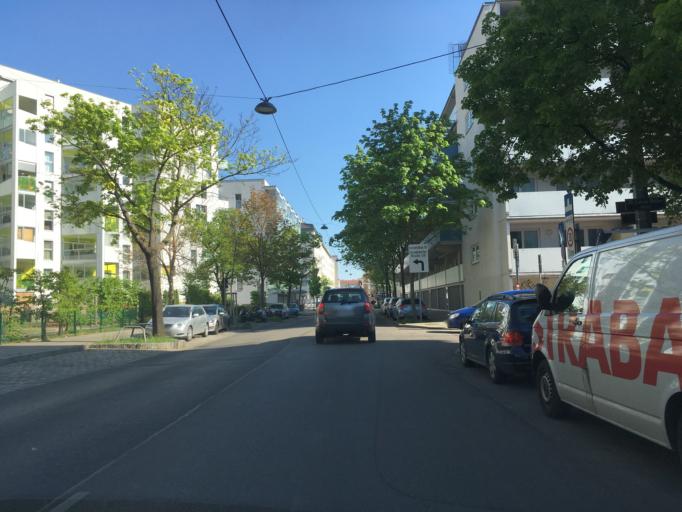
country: AT
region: Vienna
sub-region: Wien Stadt
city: Vienna
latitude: 48.2447
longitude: 16.3763
